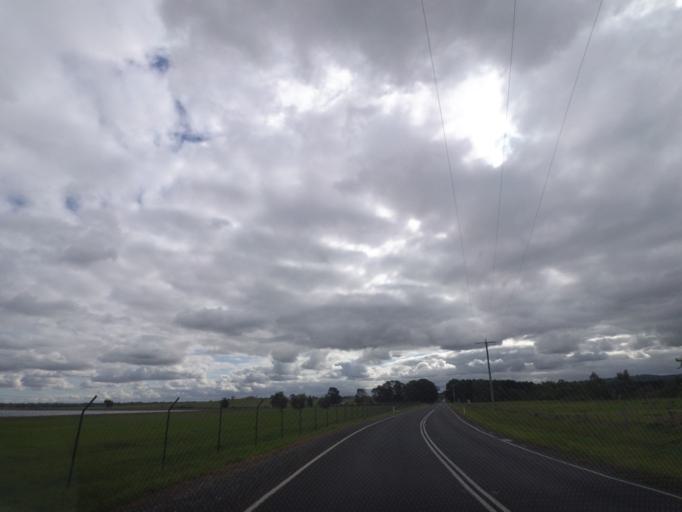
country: AU
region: Victoria
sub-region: Whittlesea
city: Whittlesea
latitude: -37.5274
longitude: 145.0980
